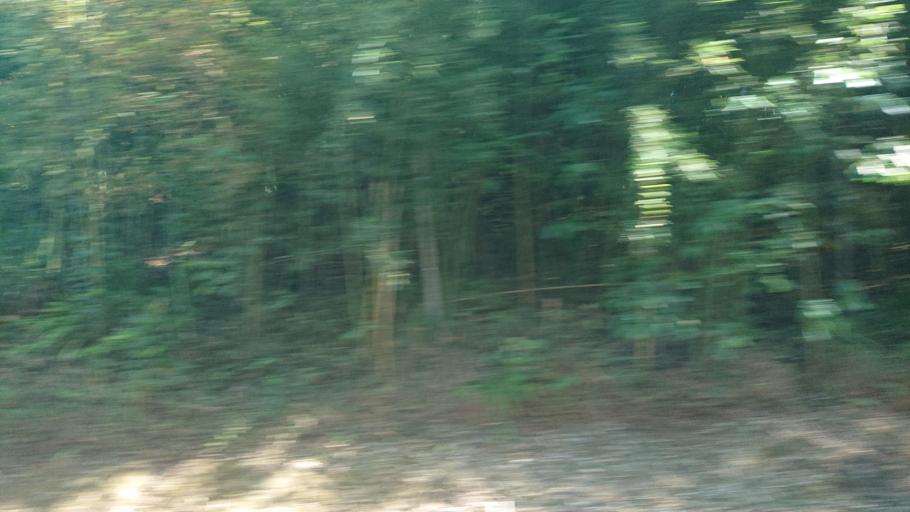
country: TW
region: Taiwan
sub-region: Chiayi
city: Jiayi Shi
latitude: 23.4703
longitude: 120.7091
